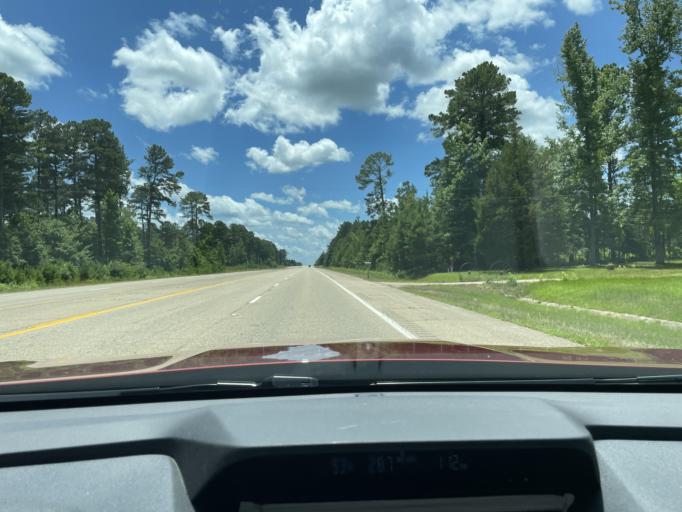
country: US
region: Arkansas
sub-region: Drew County
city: Monticello
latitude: 33.6922
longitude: -91.8063
